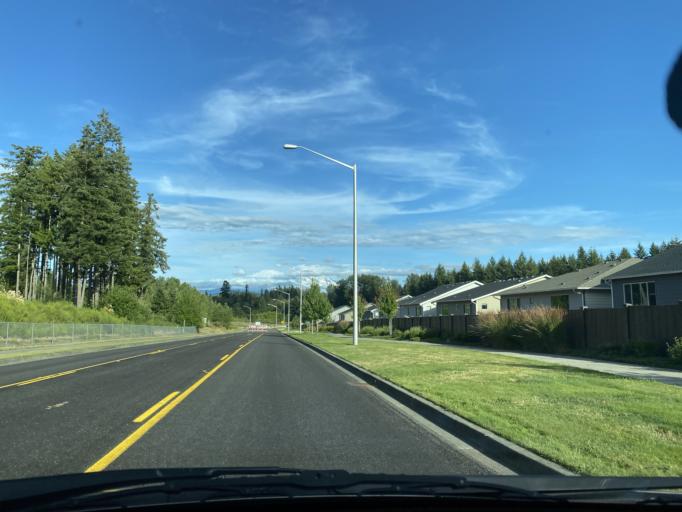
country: US
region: Washington
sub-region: Pierce County
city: Graham
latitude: 47.0872
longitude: -122.2591
